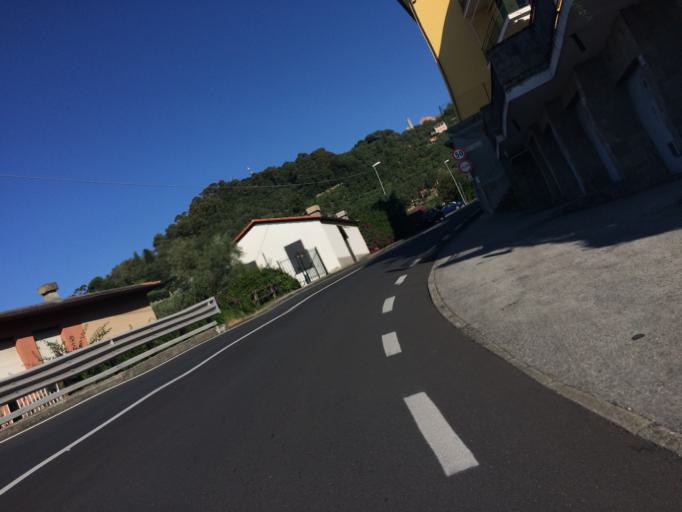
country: IT
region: Liguria
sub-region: Provincia di Genova
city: Zoagli
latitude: 44.3374
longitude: 9.2652
